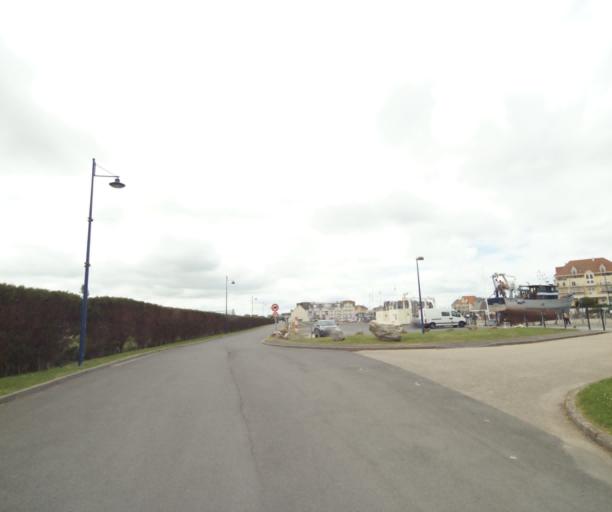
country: FR
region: Lower Normandy
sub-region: Departement du Calvados
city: Houlgate
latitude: 49.2941
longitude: -0.0930
